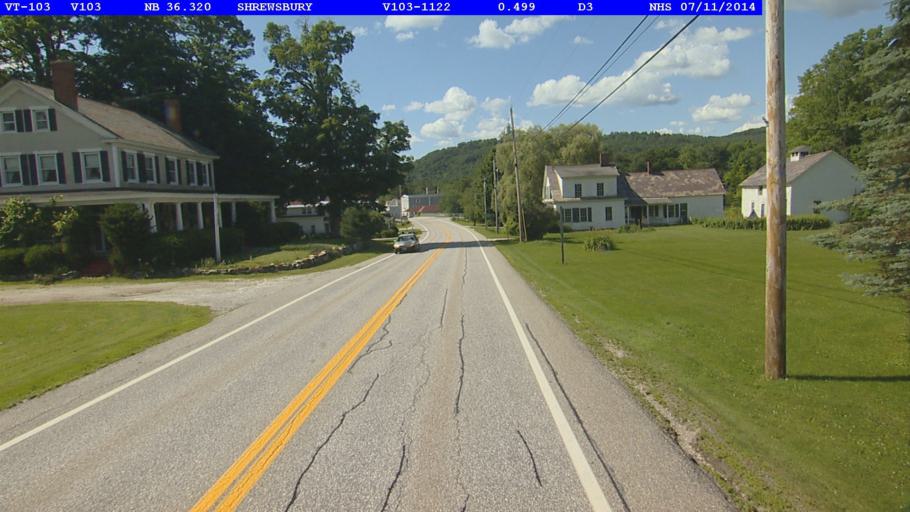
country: US
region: Vermont
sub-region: Rutland County
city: Rutland
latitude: 43.4866
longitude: -72.8802
